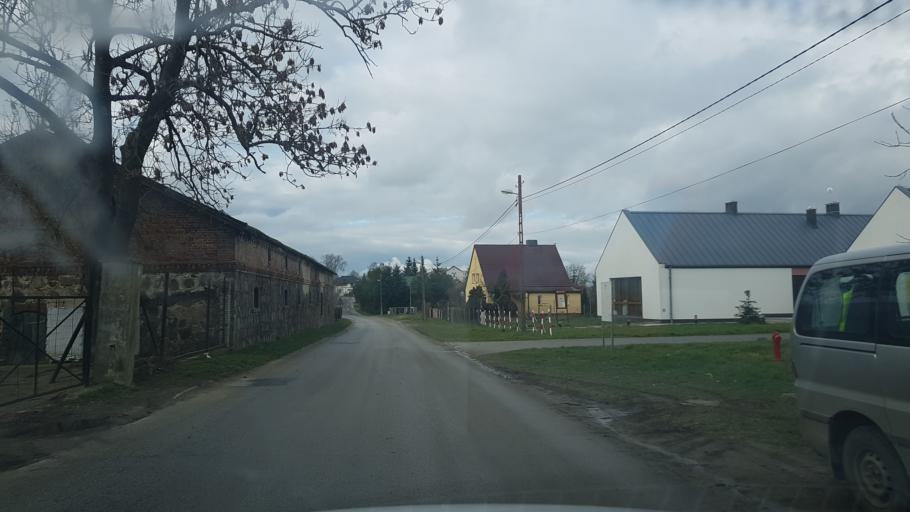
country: PL
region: West Pomeranian Voivodeship
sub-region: Powiat policki
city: Kolbaskowo
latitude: 53.3625
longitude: 14.4121
